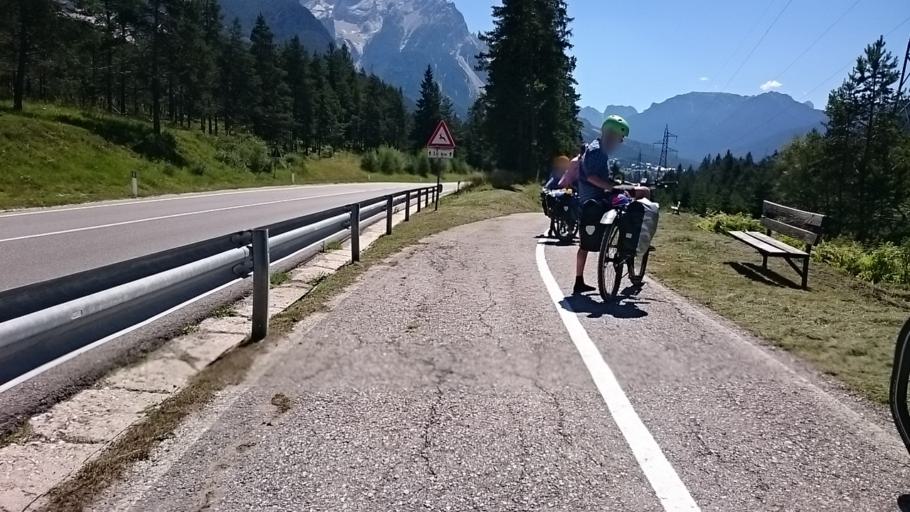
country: IT
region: Veneto
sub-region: Provincia di Belluno
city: San Vito
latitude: 46.4906
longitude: 12.1835
